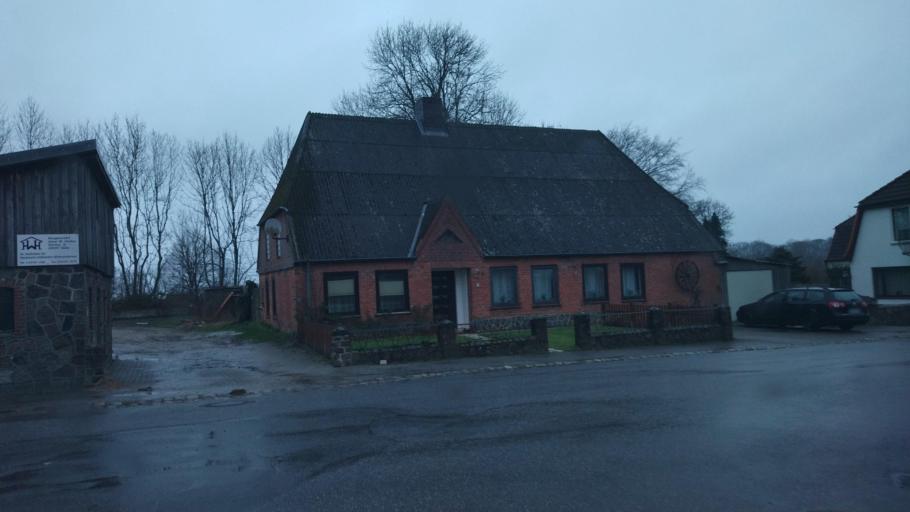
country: DE
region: Schleswig-Holstein
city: Guby
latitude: 54.4859
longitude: 9.6669
